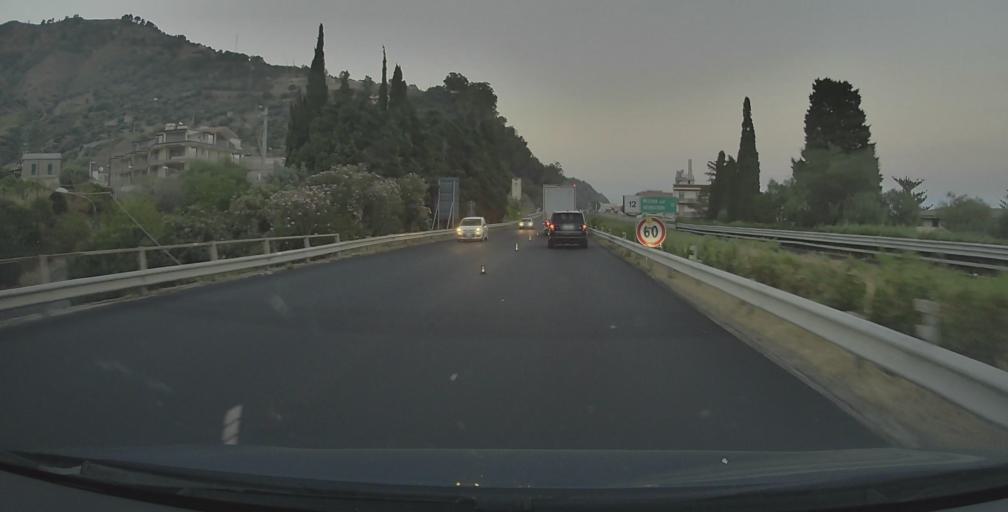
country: IT
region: Sicily
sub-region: Messina
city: Guidomandri Marina
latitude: 38.0390
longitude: 15.4537
